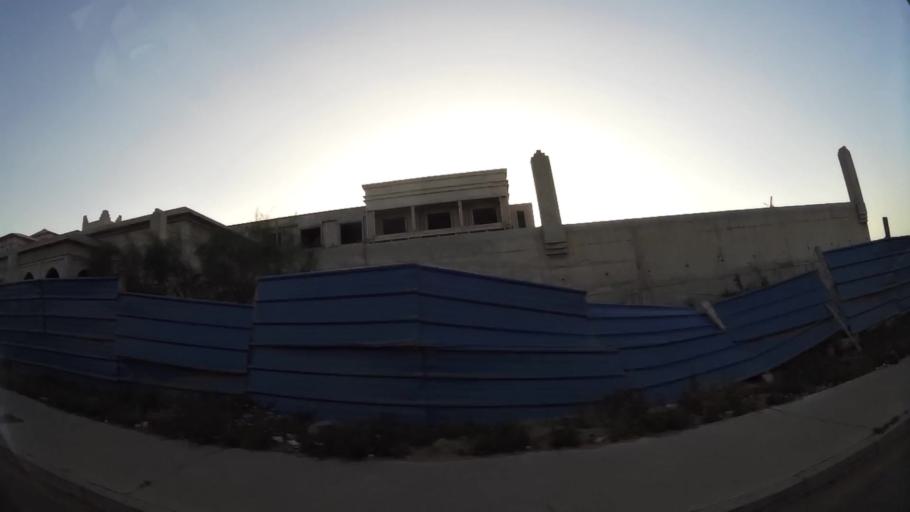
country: MA
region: Souss-Massa-Draa
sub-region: Agadir-Ida-ou-Tnan
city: Agadir
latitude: 30.4035
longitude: -9.5930
